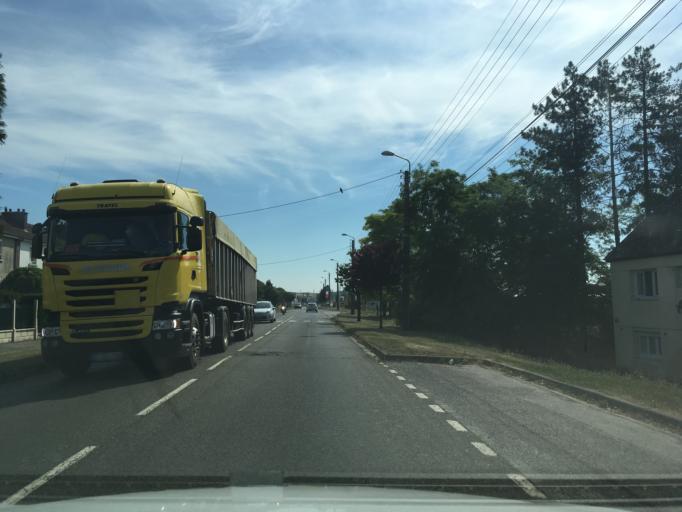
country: FR
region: Picardie
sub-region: Departement de la Somme
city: Montdidier
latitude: 49.6471
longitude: 2.5856
